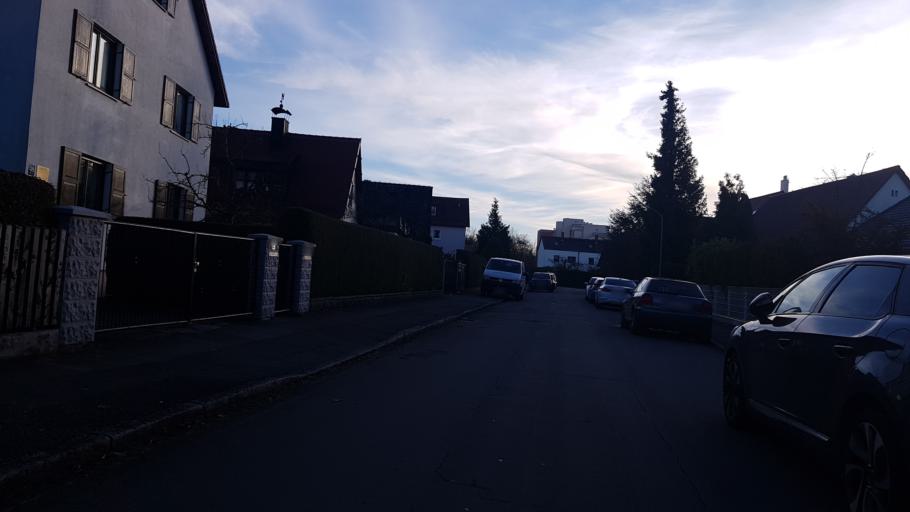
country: DE
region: Bavaria
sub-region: Upper Bavaria
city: Oberschleissheim
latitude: 48.2126
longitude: 11.5467
